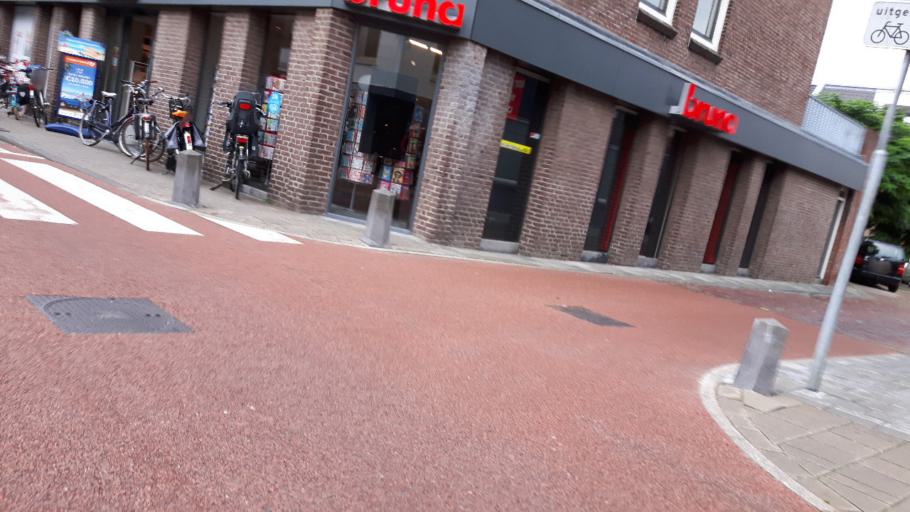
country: NL
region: Utrecht
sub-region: Stichtse Vecht
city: Maarssen
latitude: 52.1420
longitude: 5.0400
